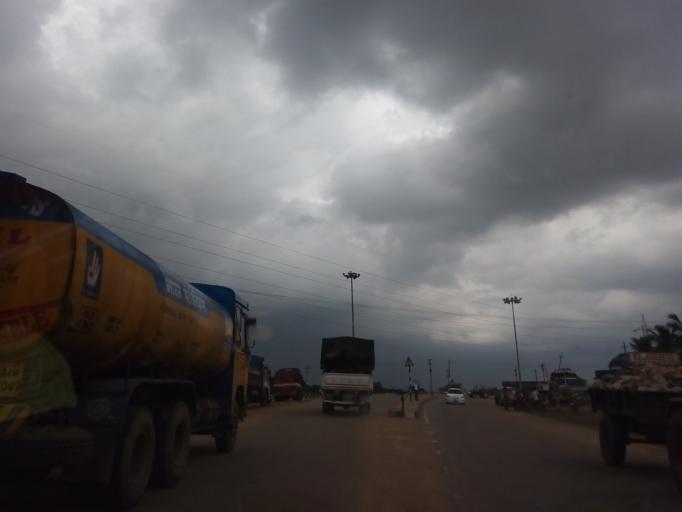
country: IN
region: Karnataka
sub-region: Hassan
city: Hassan
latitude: 12.9878
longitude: 76.1086
